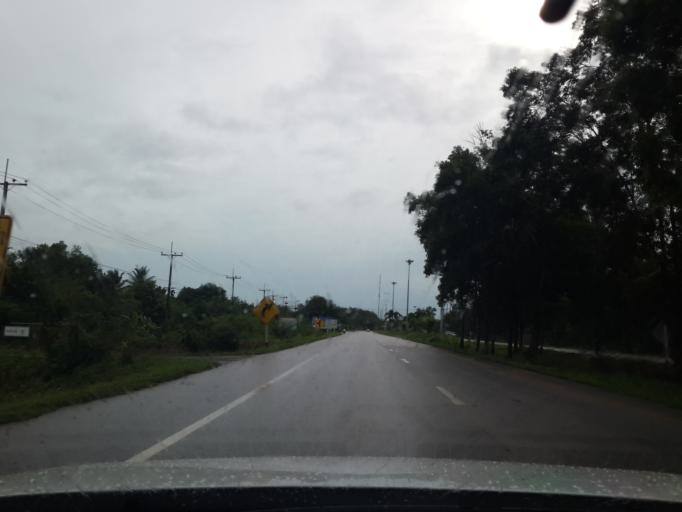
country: TH
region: Songkhla
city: Chana
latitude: 6.9814
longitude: 100.6769
